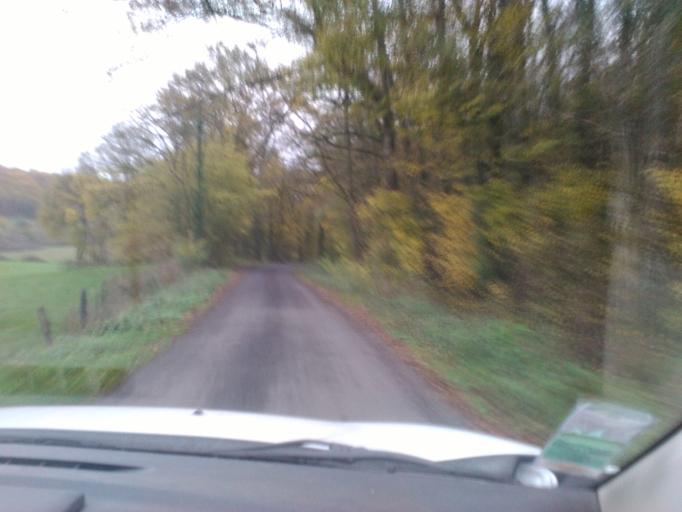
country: FR
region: Lorraine
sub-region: Departement des Vosges
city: Mirecourt
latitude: 48.2796
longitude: 6.2093
